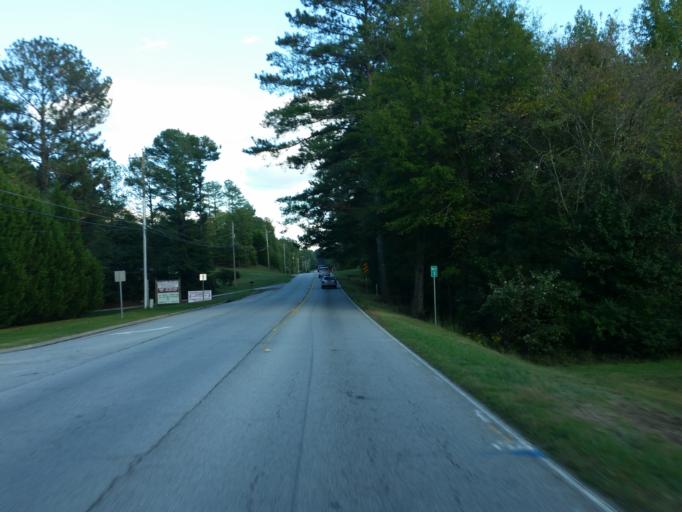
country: US
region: Georgia
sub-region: Paulding County
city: Hiram
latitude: 33.9075
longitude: -84.7414
